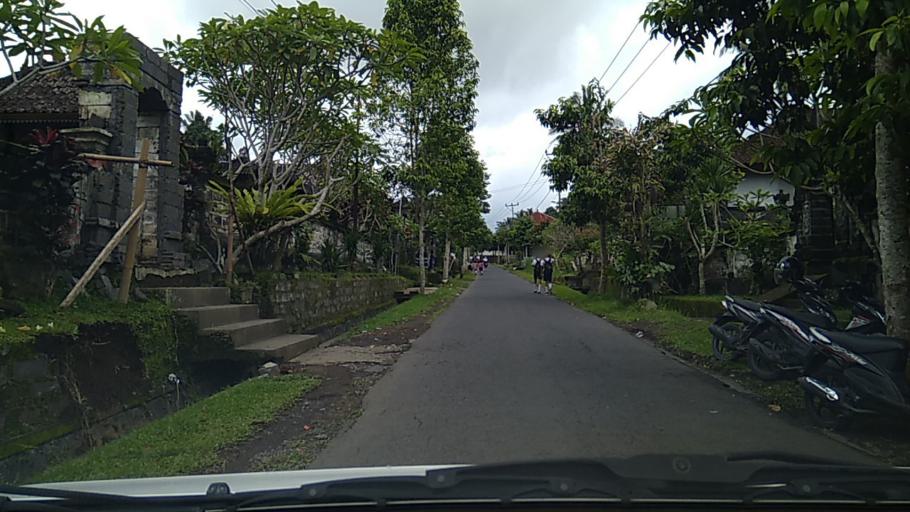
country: ID
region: Bali
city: Bangli
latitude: -8.4510
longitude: 115.3851
